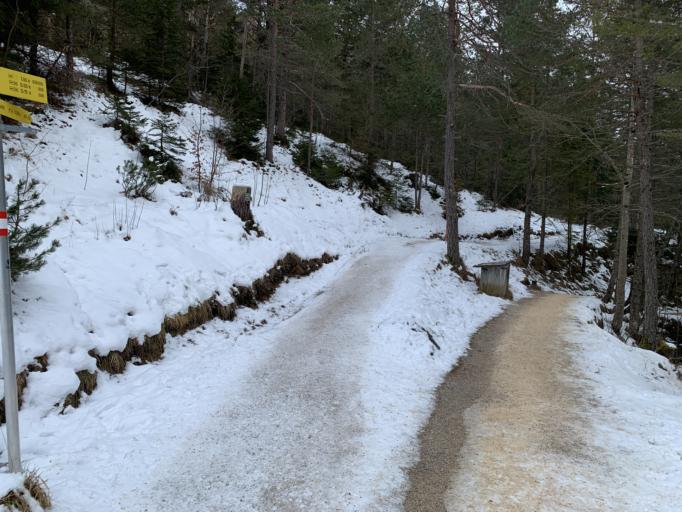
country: DE
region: Bavaria
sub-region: Upper Bavaria
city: Mittenwald
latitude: 47.4410
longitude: 11.2464
